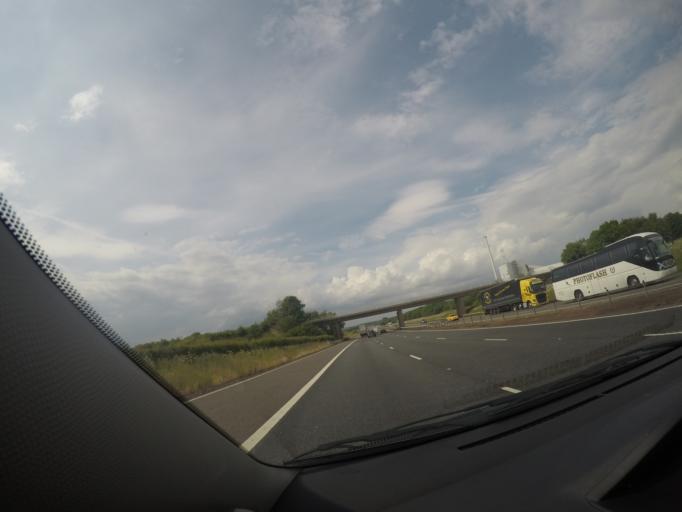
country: GB
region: Scotland
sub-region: Dumfries and Galloway
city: Lockerbie
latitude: 55.1491
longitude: -3.3822
